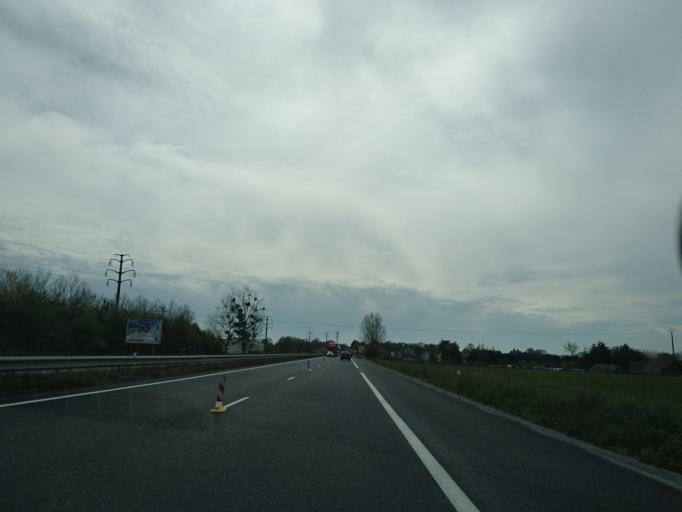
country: FR
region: Brittany
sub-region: Departement des Cotes-d'Armor
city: Quevert
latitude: 48.4641
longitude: -2.0672
